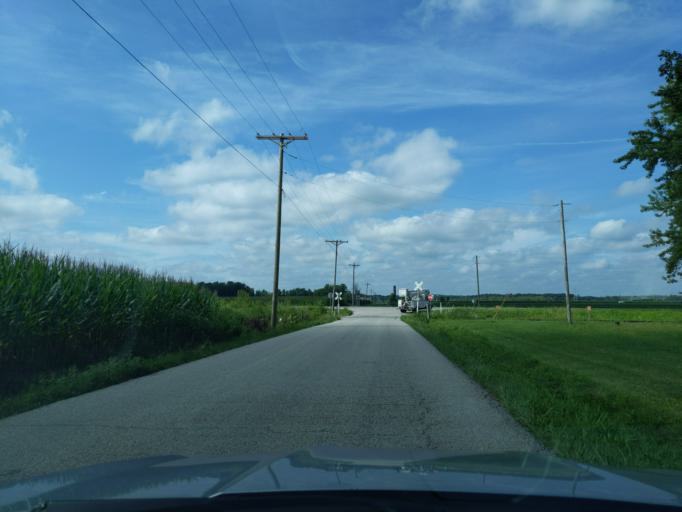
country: US
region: Indiana
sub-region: Ripley County
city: Batesville
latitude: 39.3115
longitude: -85.3477
